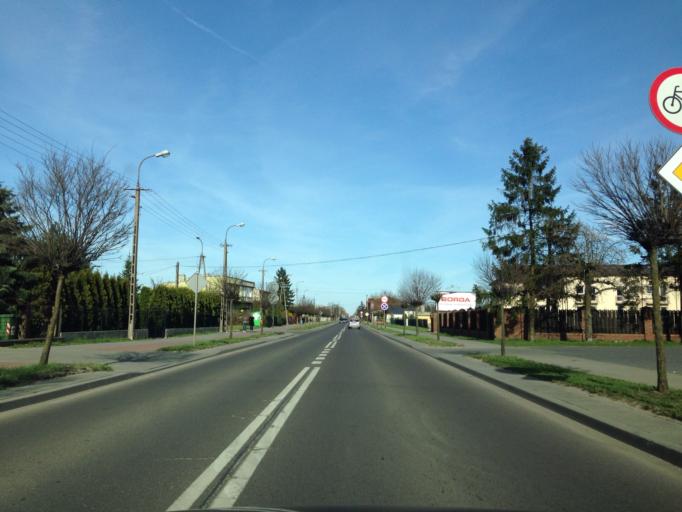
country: PL
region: Lodz Voivodeship
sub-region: Powiat leczycki
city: Leczyca
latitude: 52.0552
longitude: 19.1786
